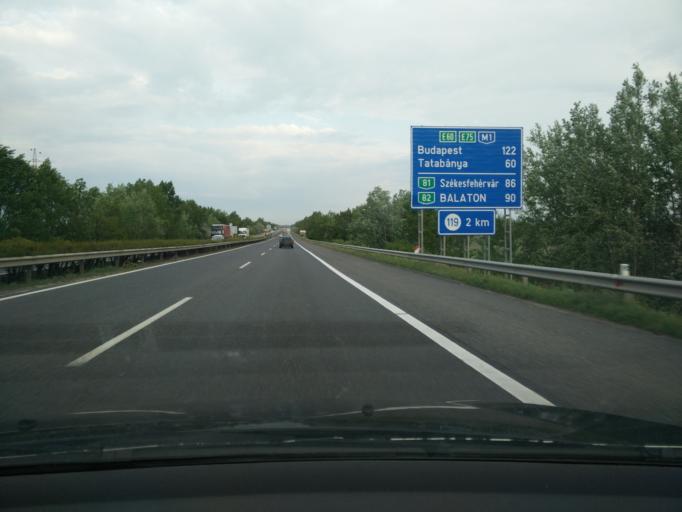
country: HU
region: Gyor-Moson-Sopron
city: Gyor
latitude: 47.6424
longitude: 17.6238
